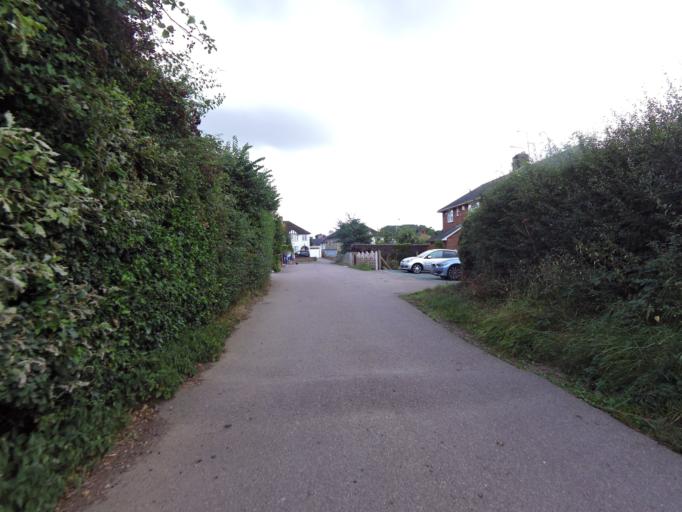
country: GB
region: England
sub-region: Hertfordshire
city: Shenley AV
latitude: 51.7176
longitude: -0.3016
